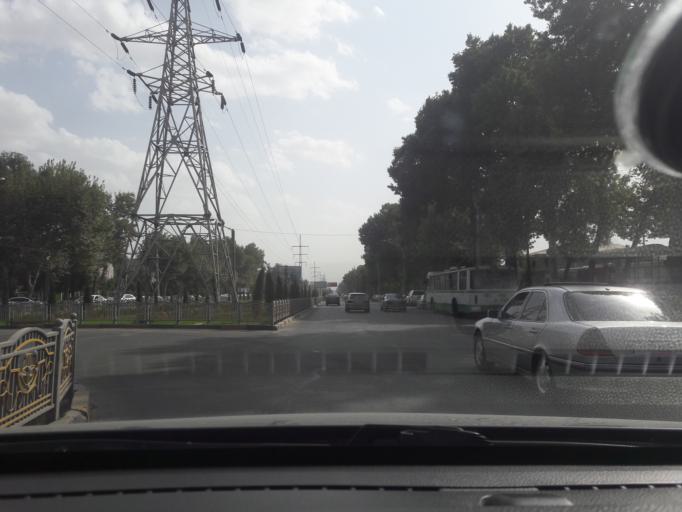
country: TJ
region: Dushanbe
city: Dushanbe
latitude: 38.5452
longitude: 68.7619
